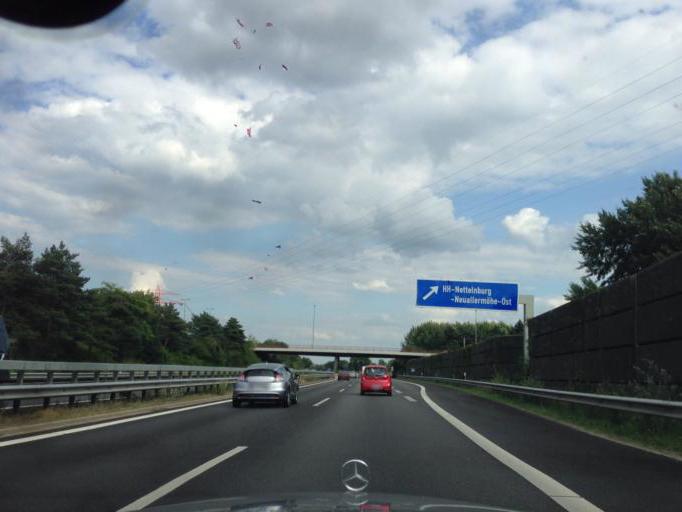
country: DE
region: Hamburg
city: Bergedorf
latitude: 53.4741
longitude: 10.1738
